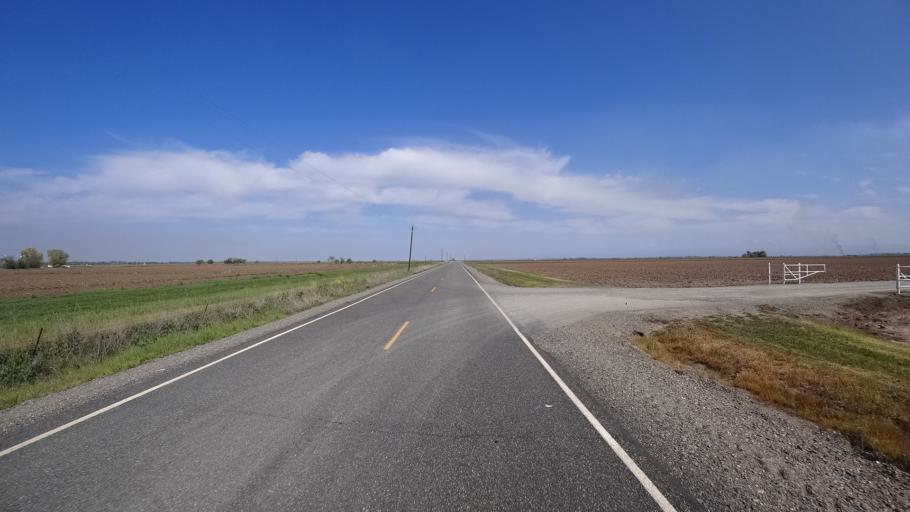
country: US
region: California
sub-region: Butte County
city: Durham
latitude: 39.4954
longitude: -121.9299
